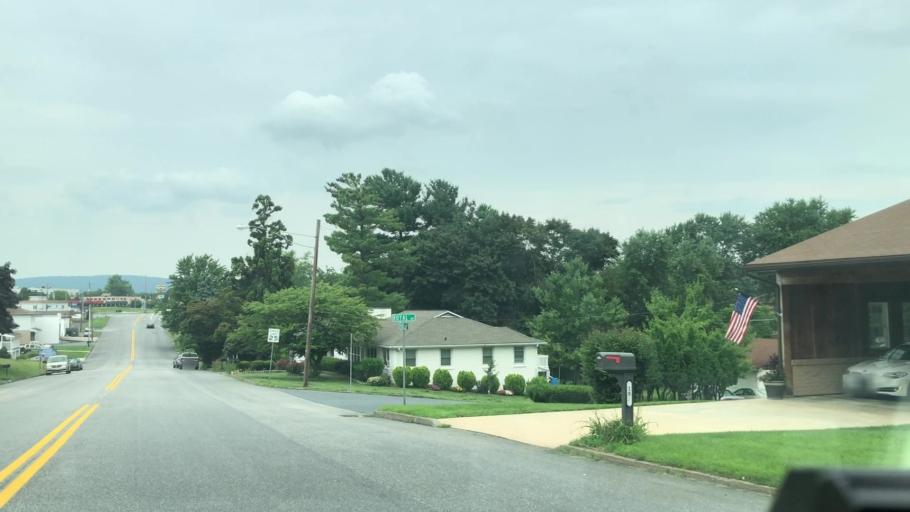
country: US
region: Pennsylvania
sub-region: Dauphin County
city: Colonial Park
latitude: 40.3004
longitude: -76.8088
